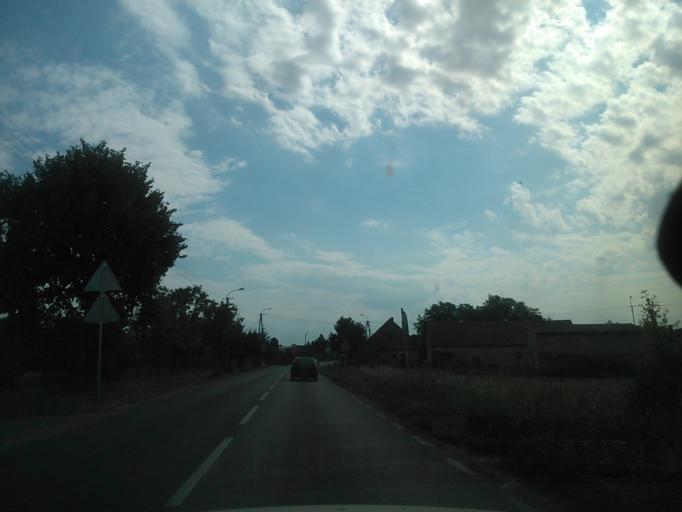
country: PL
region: Warmian-Masurian Voivodeship
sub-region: Powiat dzialdowski
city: Ilowo -Osada
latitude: 53.1782
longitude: 20.2952
